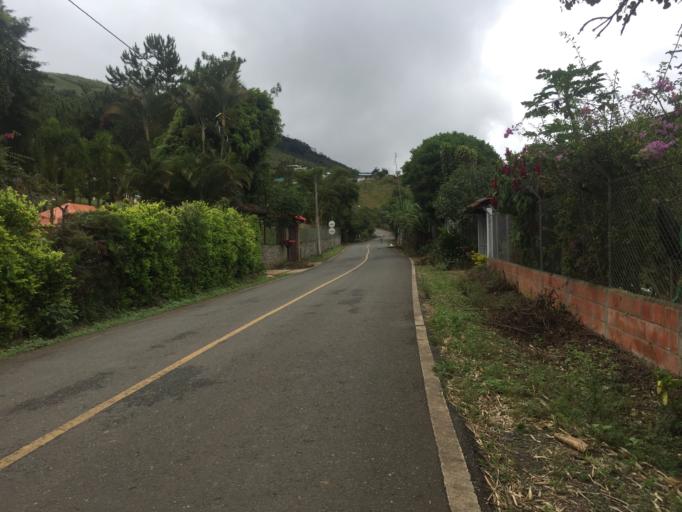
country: CO
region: Valle del Cauca
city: Dagua
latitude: 3.6953
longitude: -76.5890
